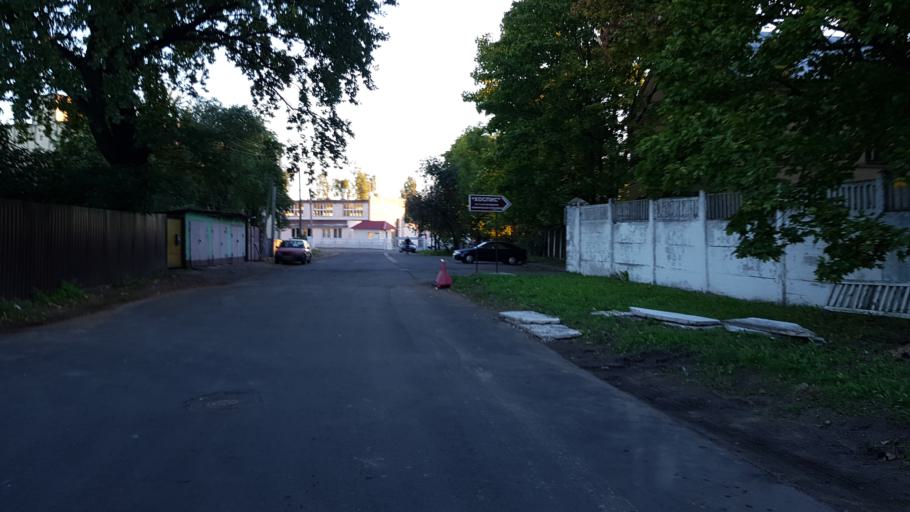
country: BY
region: Minsk
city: Syenitsa
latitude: 53.8770
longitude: 27.5210
